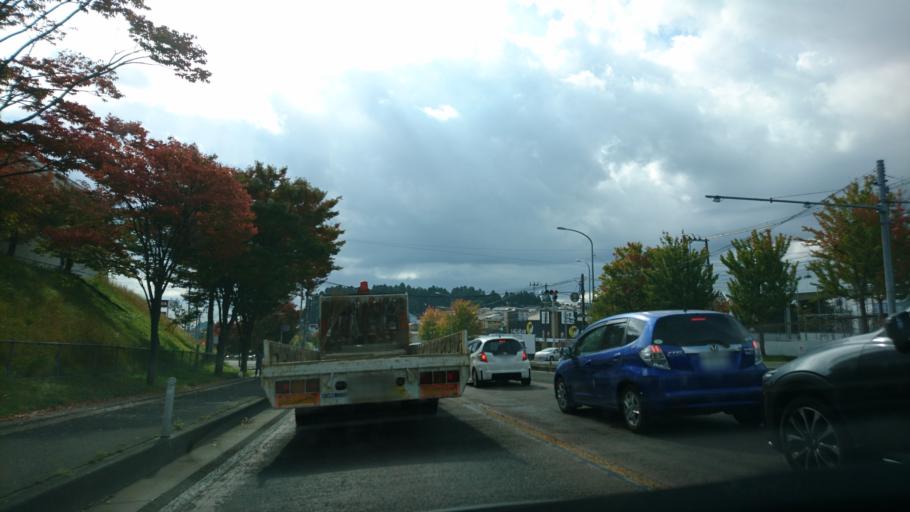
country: JP
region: Miyagi
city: Tomiya
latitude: 38.3541
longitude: 140.8710
